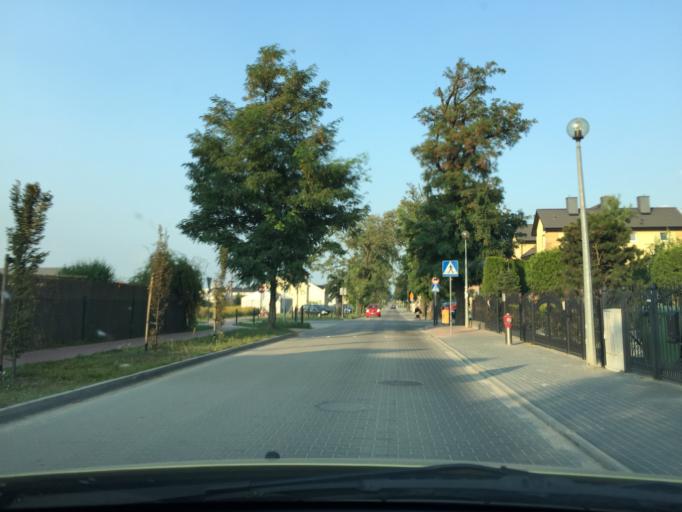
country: PL
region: Greater Poland Voivodeship
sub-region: Powiat poznanski
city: Plewiska
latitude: 52.3736
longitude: 16.8115
